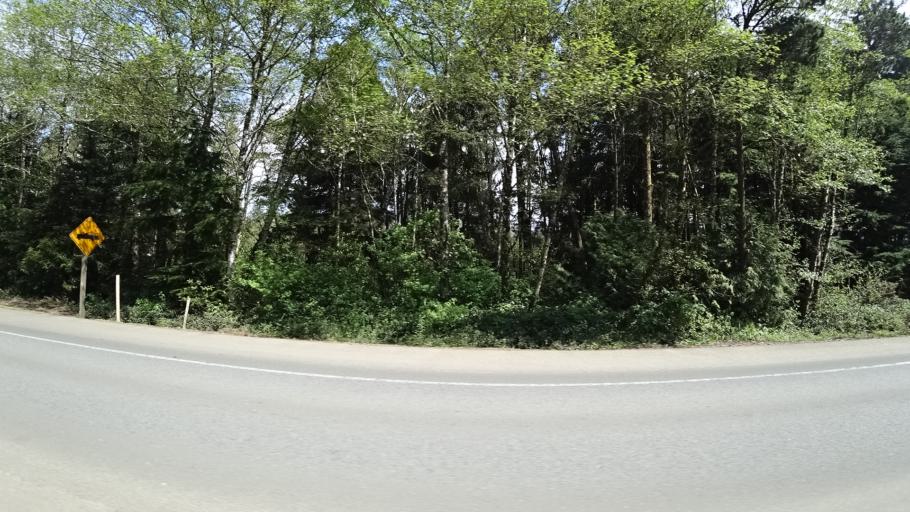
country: US
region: Oregon
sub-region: Lincoln County
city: Lincoln Beach
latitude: 44.8736
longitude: -124.0340
